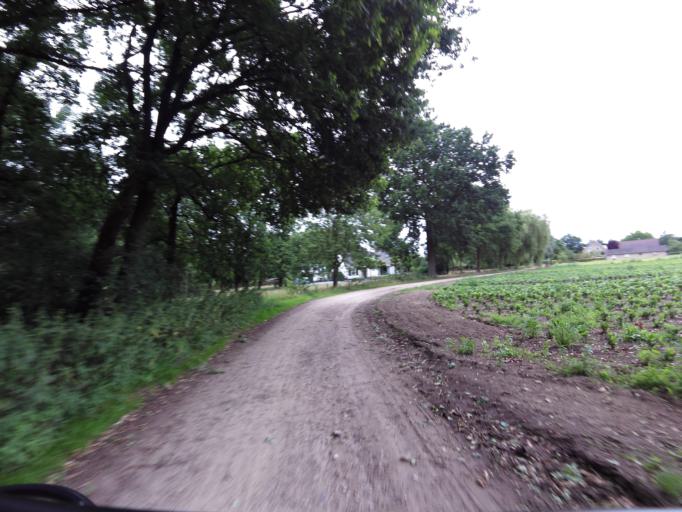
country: NL
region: North Brabant
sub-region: Gemeente Son en Breugel
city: Breugel
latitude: 51.5401
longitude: 5.4996
